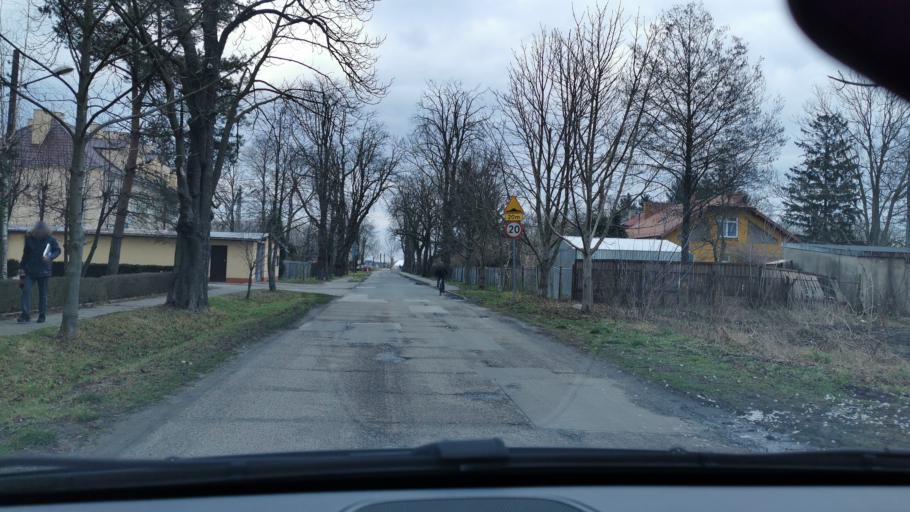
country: PL
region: Masovian Voivodeship
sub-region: Powiat zyrardowski
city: Guzow
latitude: 52.1157
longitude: 20.3271
